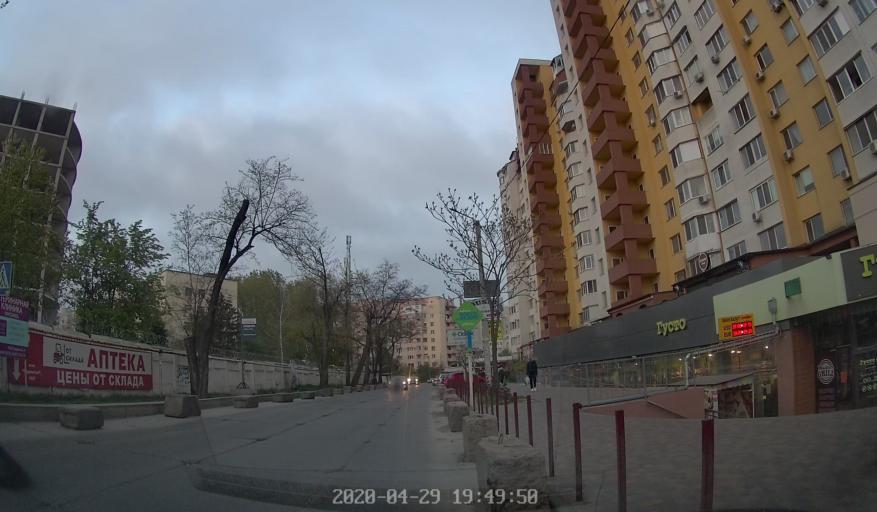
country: NE
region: Zinder
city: Mirriah
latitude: 13.9214
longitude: 9.2117
